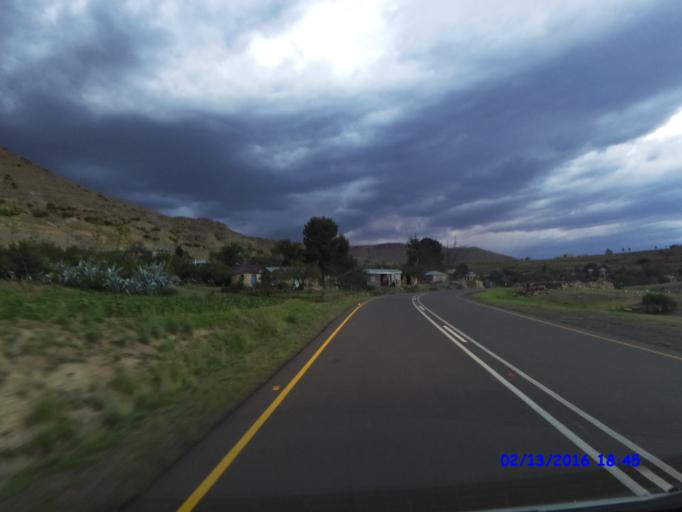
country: LS
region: Qacha's Nek
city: Qacha's Nek
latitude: -30.0567
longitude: 28.3002
